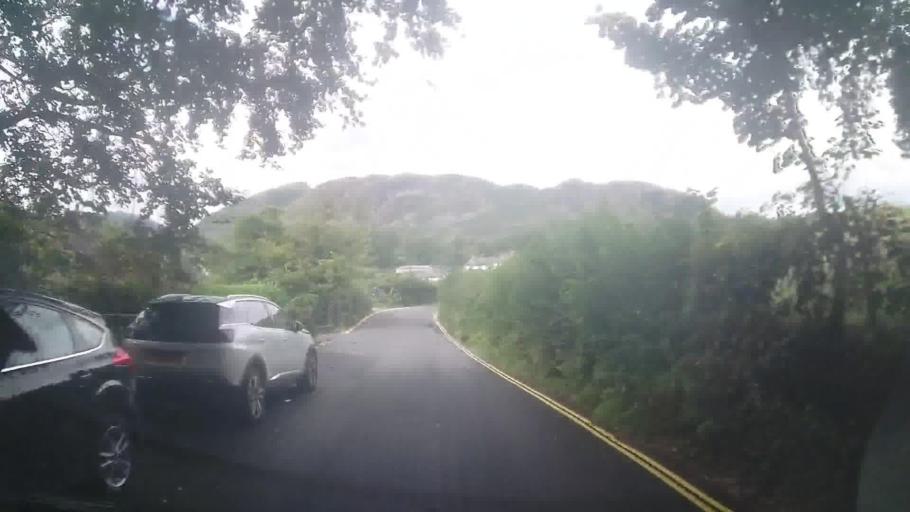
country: GB
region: England
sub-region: Cumbria
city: Ambleside
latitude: 54.4204
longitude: -3.0510
